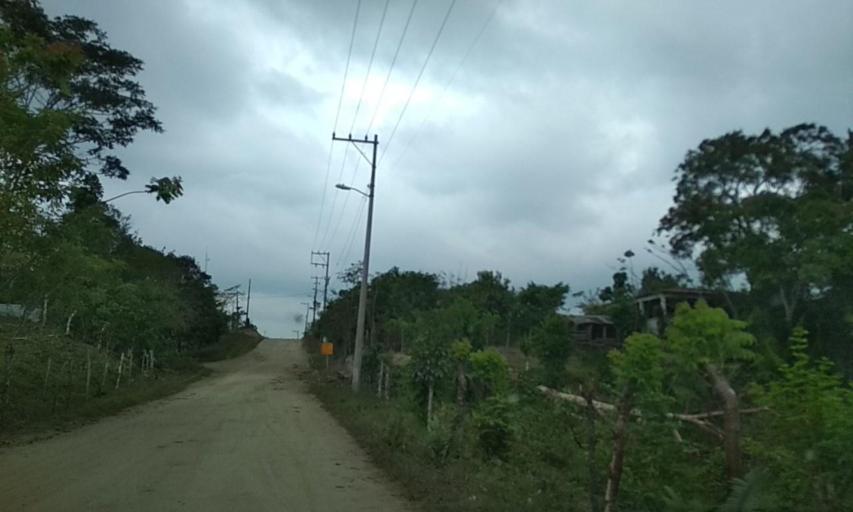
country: MX
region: Tabasco
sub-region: Huimanguillo
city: Francisco Rueda
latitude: 17.6544
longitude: -94.0952
